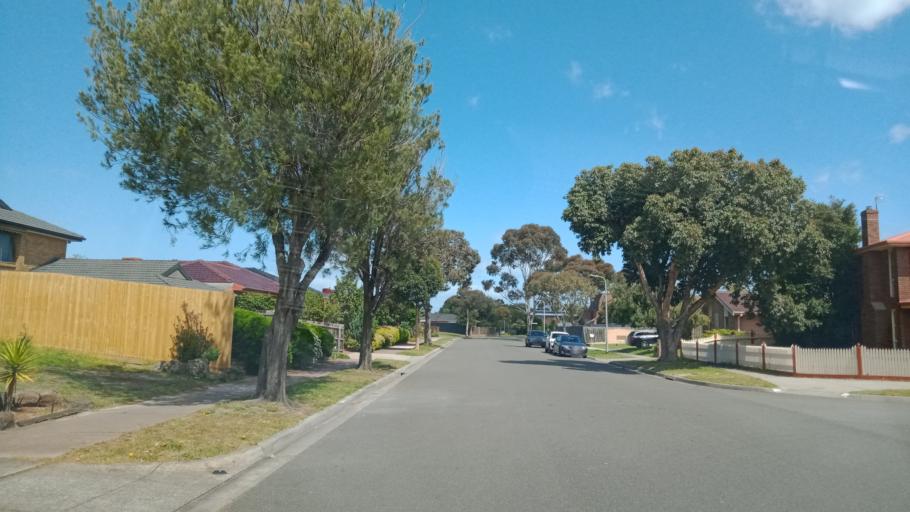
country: AU
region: Victoria
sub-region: Kingston
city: Chelsea Heights
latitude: -38.0339
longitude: 145.1336
